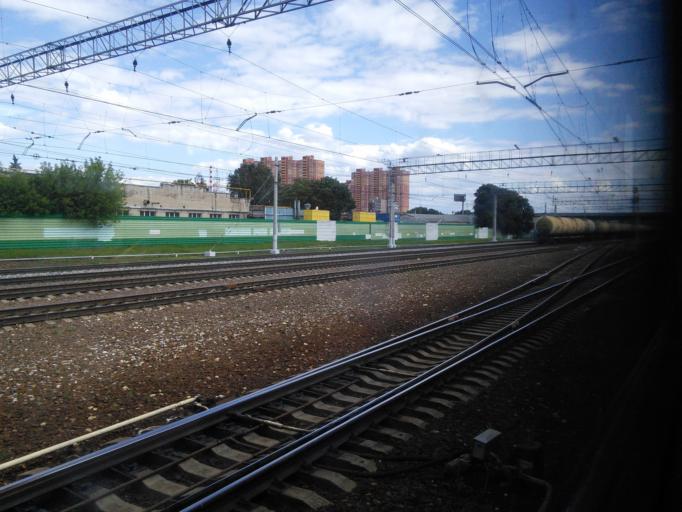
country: RU
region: Moskovskaya
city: Lyubertsy
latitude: 55.6859
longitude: 37.8896
